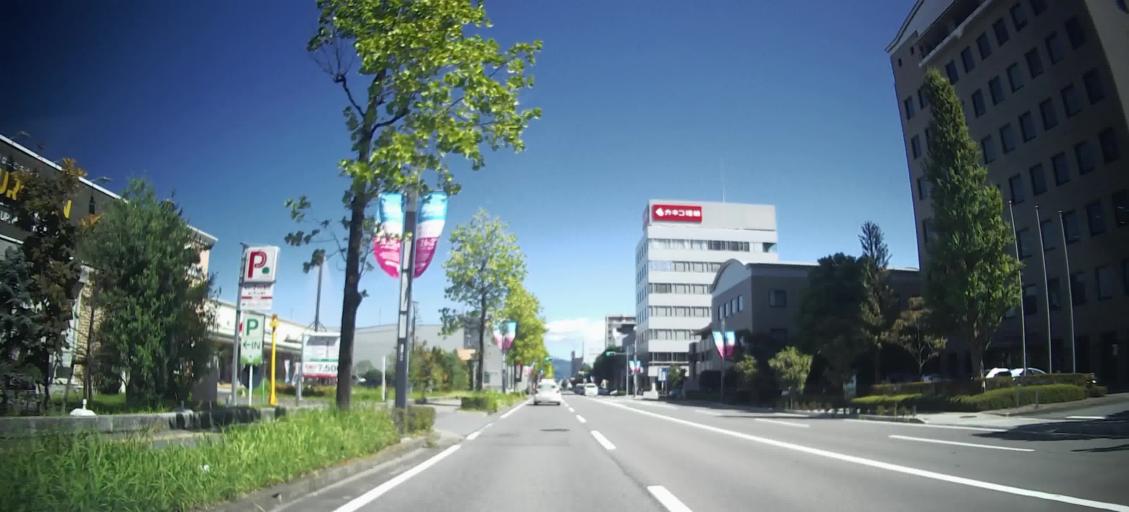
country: JP
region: Gunma
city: Maebashi-shi
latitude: 36.3759
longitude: 139.0457
